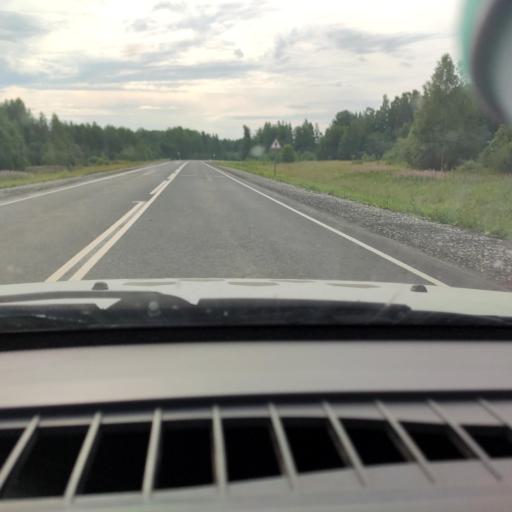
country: RU
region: Kirov
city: Kostino
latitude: 58.6514
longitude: 53.7853
